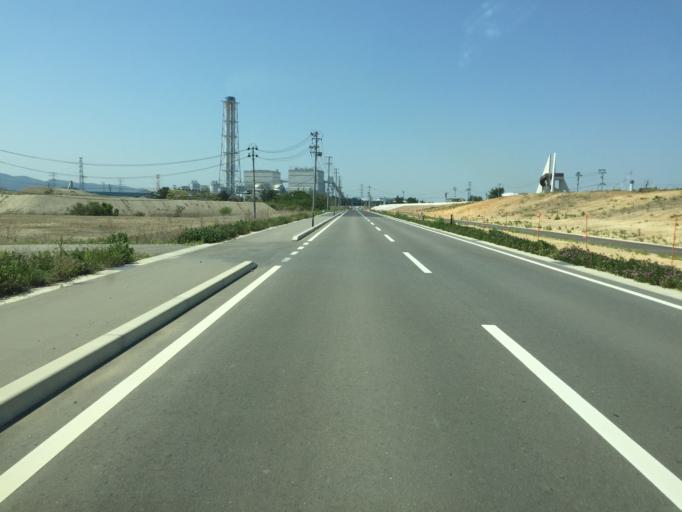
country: JP
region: Miyagi
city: Marumori
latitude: 37.8332
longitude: 140.9541
